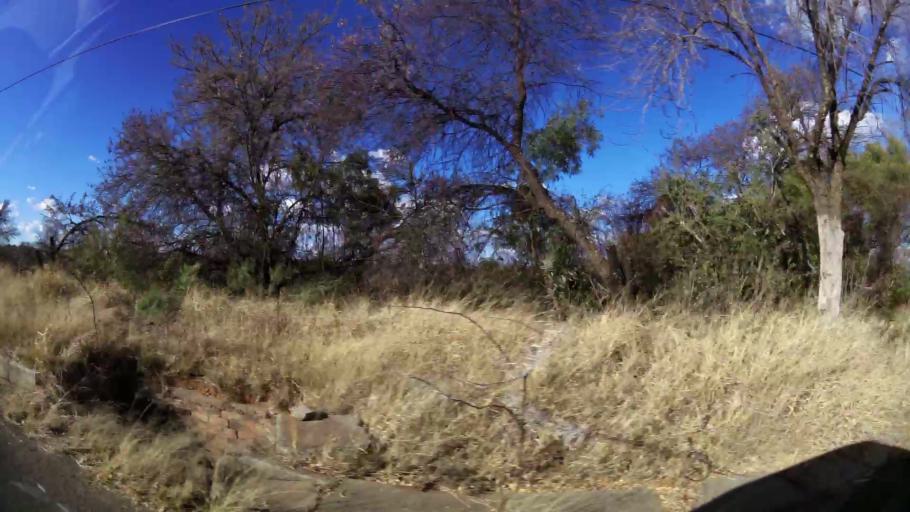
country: ZA
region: North-West
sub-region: Dr Kenneth Kaunda District Municipality
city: Klerksdorp
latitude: -26.8362
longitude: 26.6623
